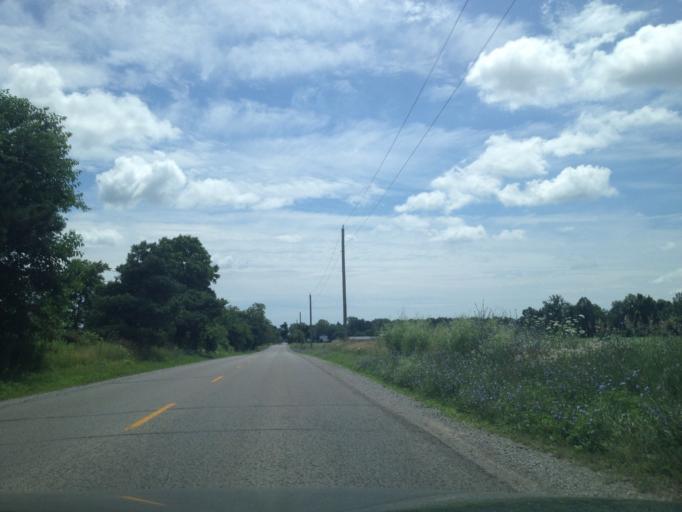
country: CA
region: Ontario
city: Norfolk County
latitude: 42.8139
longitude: -80.3234
